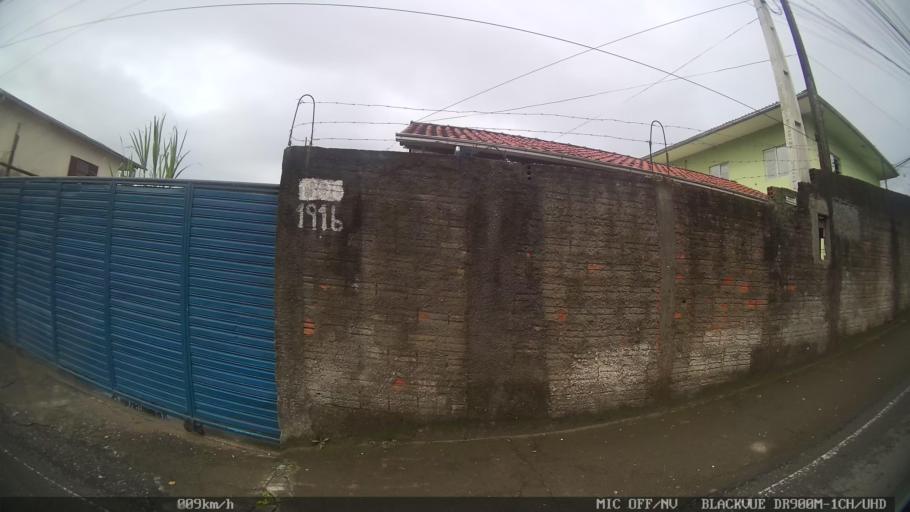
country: BR
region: Santa Catarina
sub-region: Biguacu
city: Biguacu
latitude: -27.5363
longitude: -48.6466
